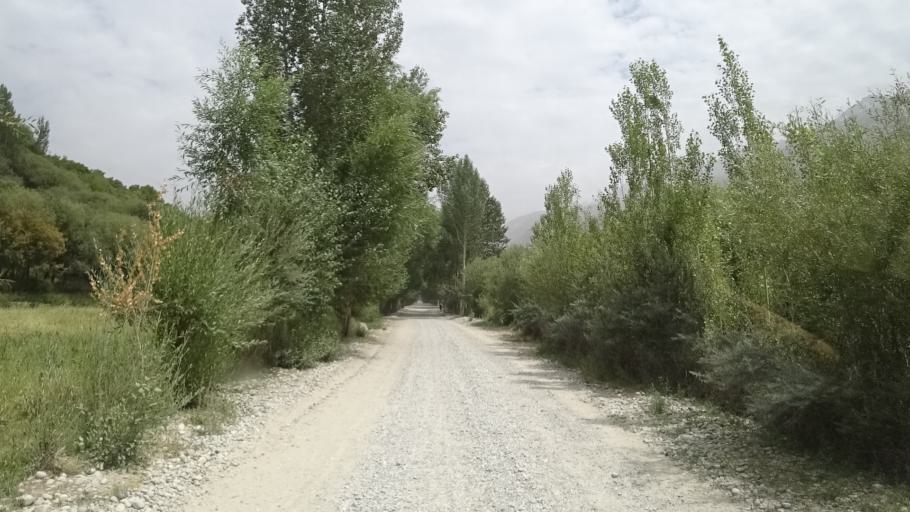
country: AF
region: Badakhshan
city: Khandud
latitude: 37.0447
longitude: 72.6671
